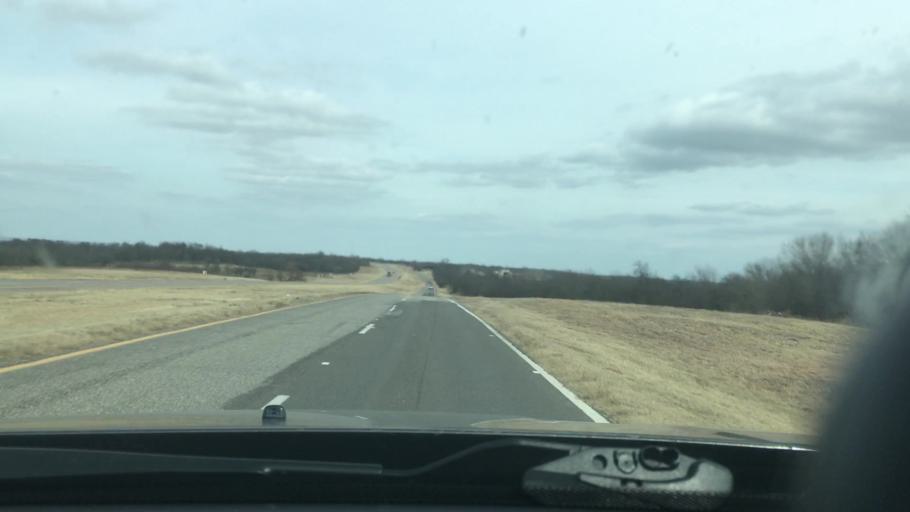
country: US
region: Oklahoma
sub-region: Pontotoc County
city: Ada
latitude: 34.6925
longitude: -96.7419
